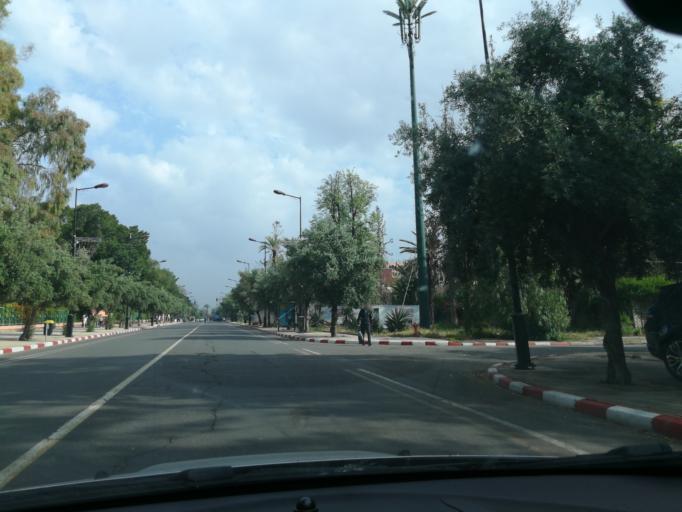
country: MA
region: Marrakech-Tensift-Al Haouz
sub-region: Marrakech
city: Marrakesh
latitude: 31.6227
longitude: -8.0078
